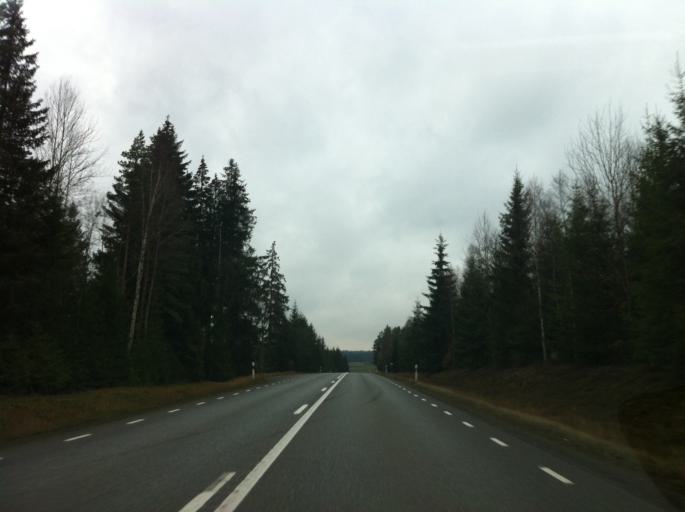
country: SE
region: Joenkoeping
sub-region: Vetlanda Kommun
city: Landsbro
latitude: 57.3980
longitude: 14.8759
